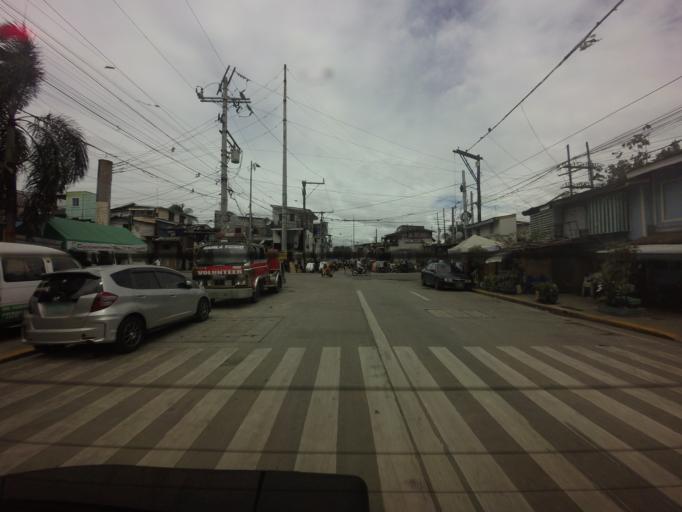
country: PH
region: Metro Manila
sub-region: City of Manila
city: Manila
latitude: 14.6197
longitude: 120.9743
